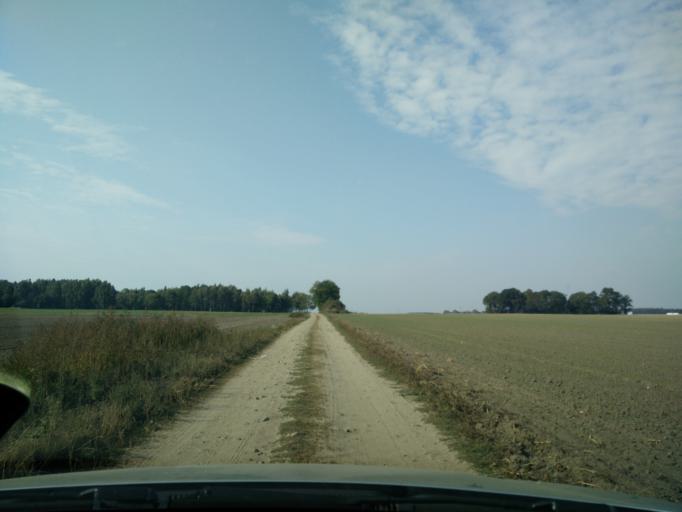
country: PL
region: Greater Poland Voivodeship
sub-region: Powiat sredzki
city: Sroda Wielkopolska
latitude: 52.3061
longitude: 17.2636
